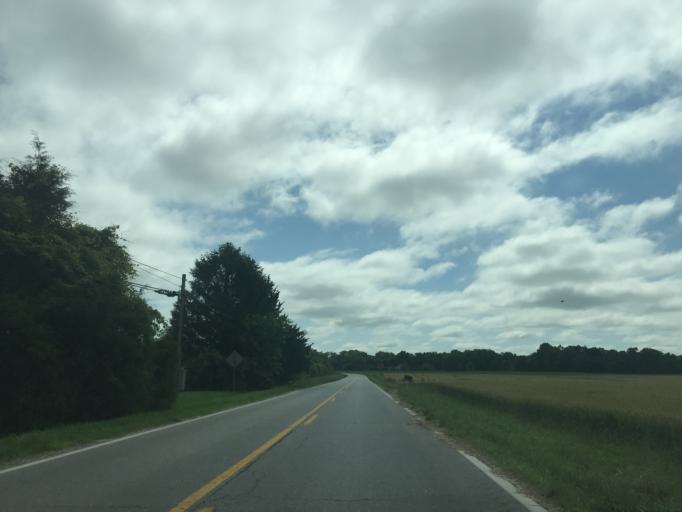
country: US
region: Maryland
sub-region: Caroline County
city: Ridgely
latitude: 38.9168
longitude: -75.9358
